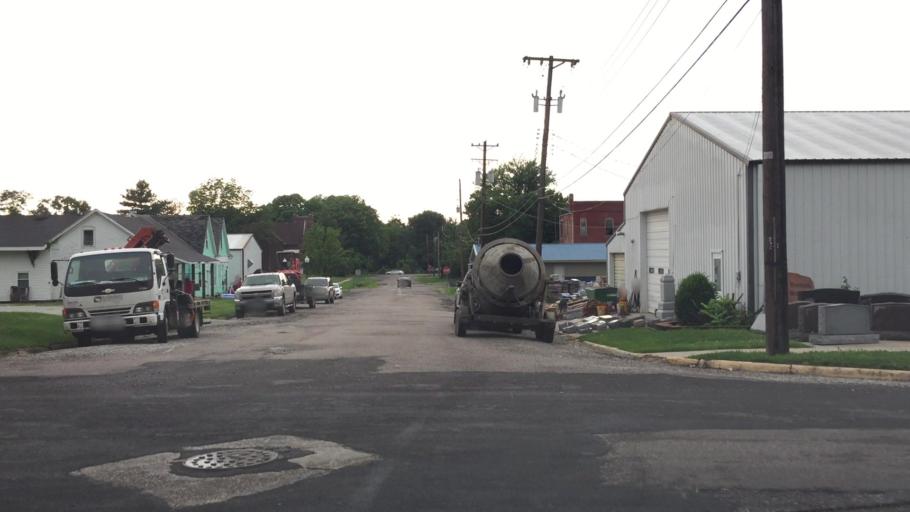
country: US
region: Illinois
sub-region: Hancock County
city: Warsaw
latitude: 40.3586
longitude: -91.4347
